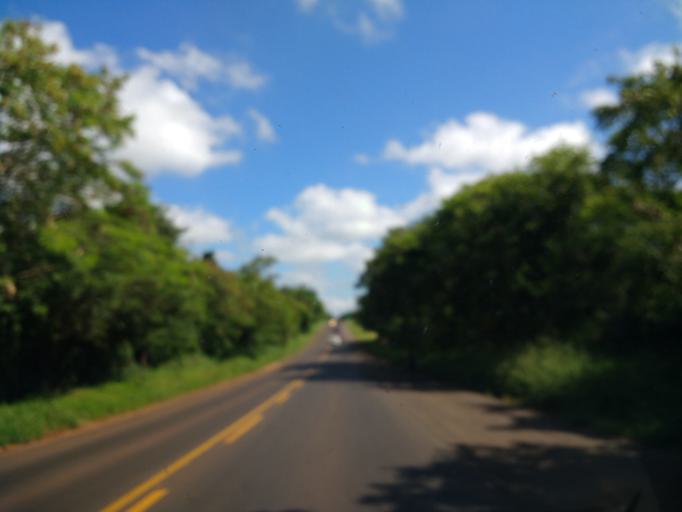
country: BR
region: Parana
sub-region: Umuarama
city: Umuarama
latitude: -23.8194
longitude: -53.3341
